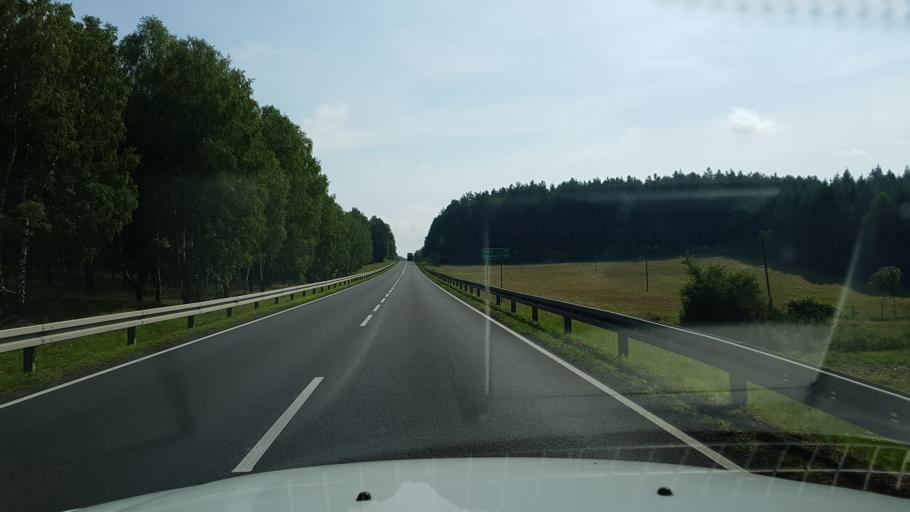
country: PL
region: West Pomeranian Voivodeship
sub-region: Powiat walecki
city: Miroslawiec
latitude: 53.3496
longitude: 16.1214
